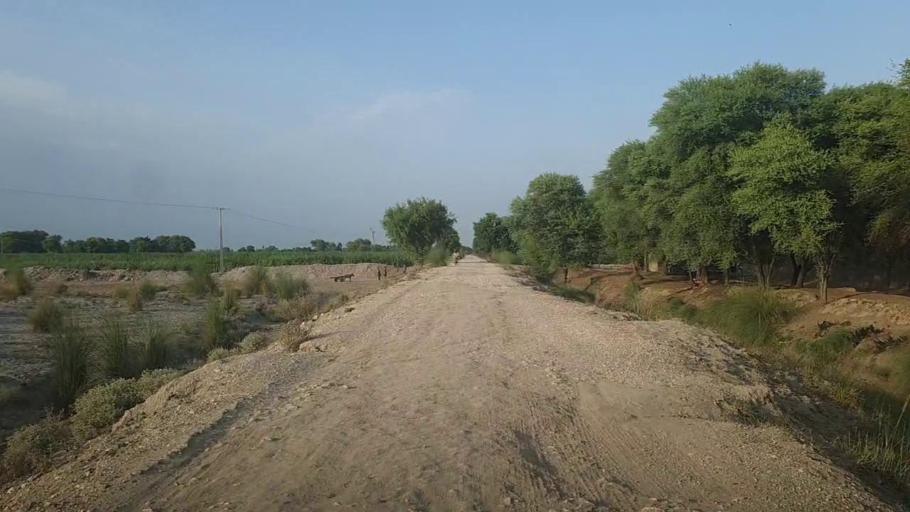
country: PK
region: Sindh
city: Ubauro
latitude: 28.3674
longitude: 69.7966
